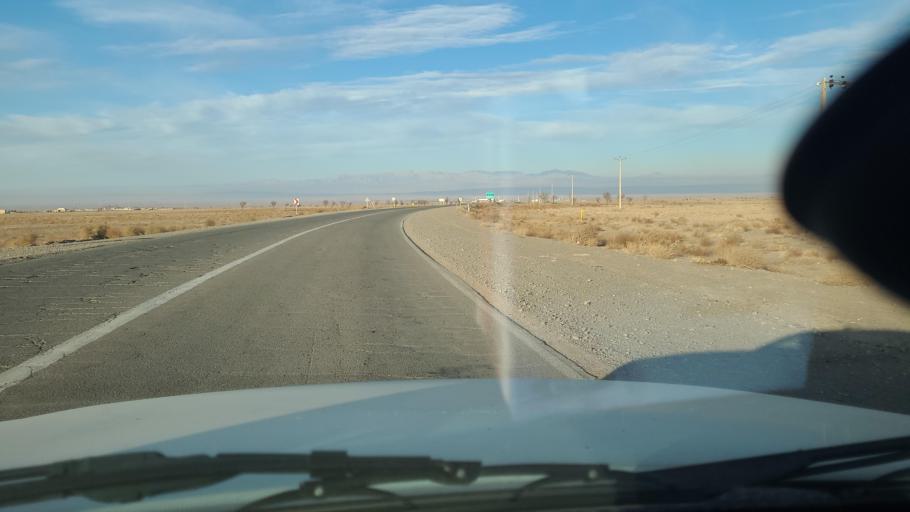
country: IR
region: Razavi Khorasan
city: Neqab
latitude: 36.4997
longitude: 57.5310
